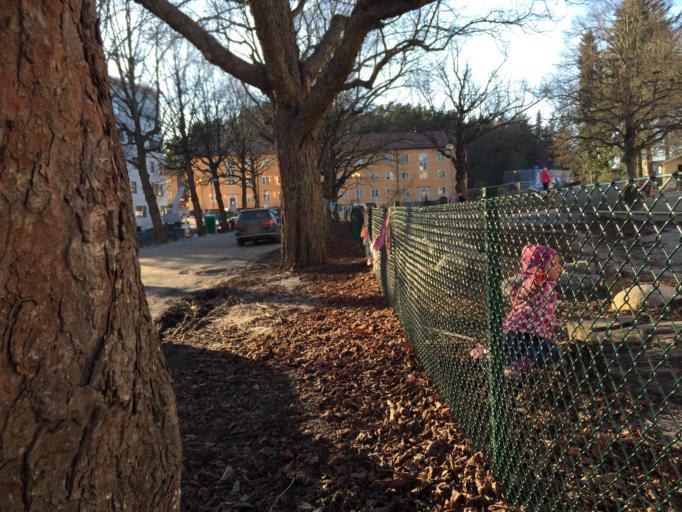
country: SE
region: Stockholm
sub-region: Stockholms Kommun
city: Bromma
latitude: 59.3565
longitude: 17.9002
